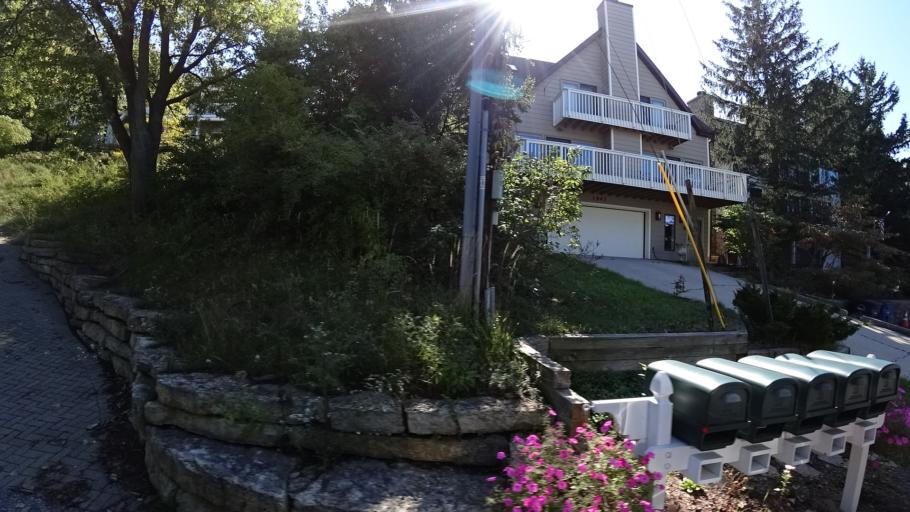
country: US
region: Indiana
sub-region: LaPorte County
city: Long Beach
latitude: 41.7365
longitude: -86.8754
